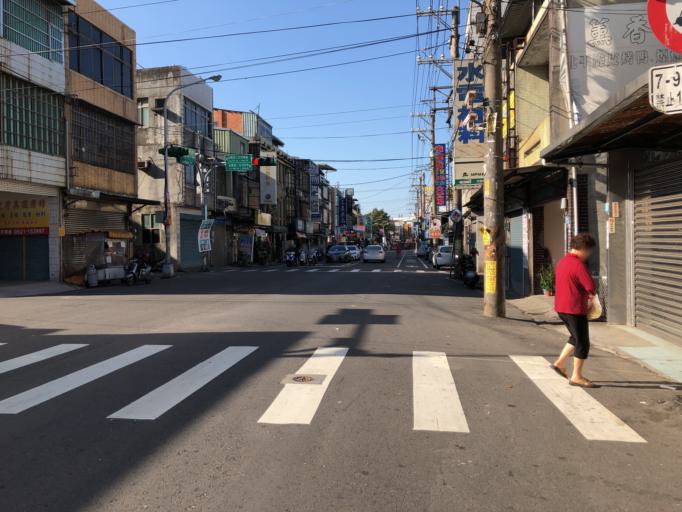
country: TW
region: Taiwan
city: Daxi
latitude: 24.9306
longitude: 121.2266
